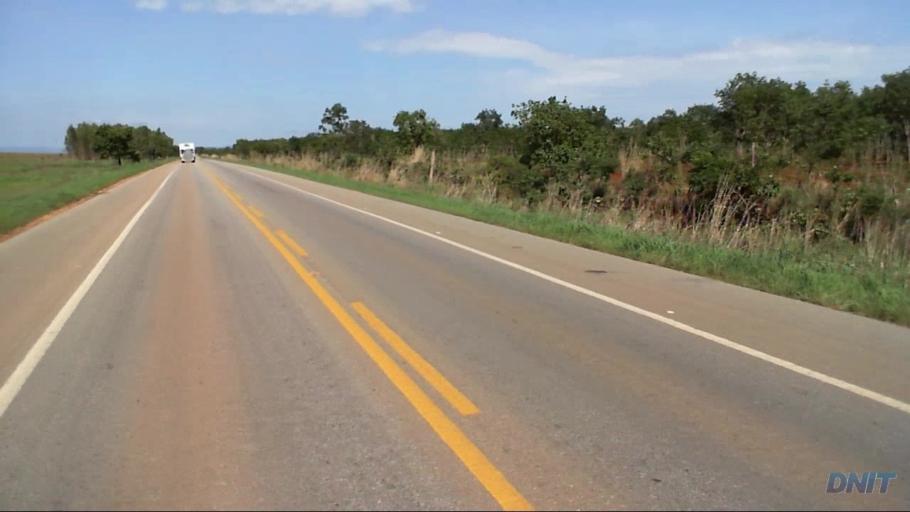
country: BR
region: Goias
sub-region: Barro Alto
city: Barro Alto
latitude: -15.2061
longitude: -48.7212
